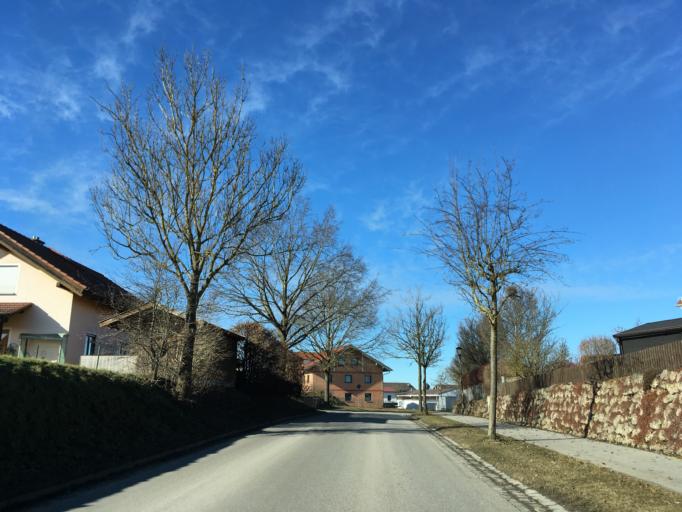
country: DE
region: Bavaria
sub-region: Upper Bavaria
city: Obertaufkirchen
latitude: 48.2599
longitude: 12.2825
